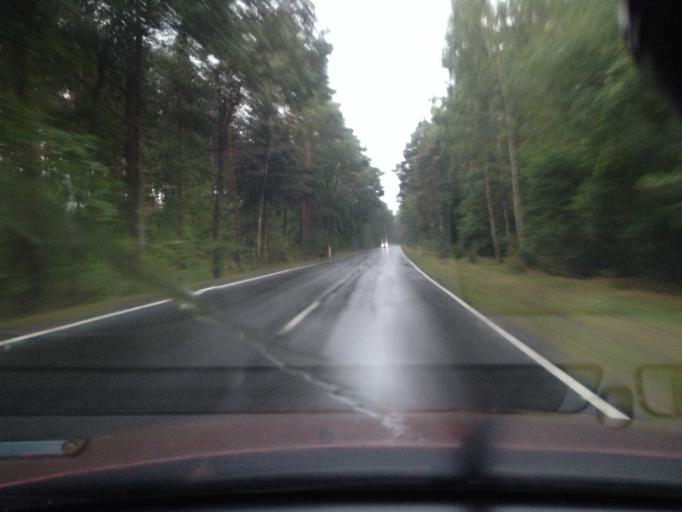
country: PL
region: Lubusz
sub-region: Powiat zaganski
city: Ilowa
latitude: 51.4483
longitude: 15.1987
